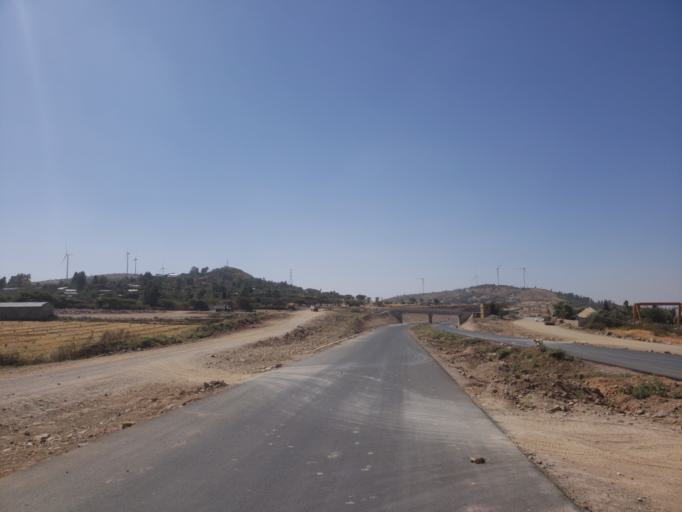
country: ET
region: Oromiya
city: Mojo
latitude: 8.5703
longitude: 39.1668
